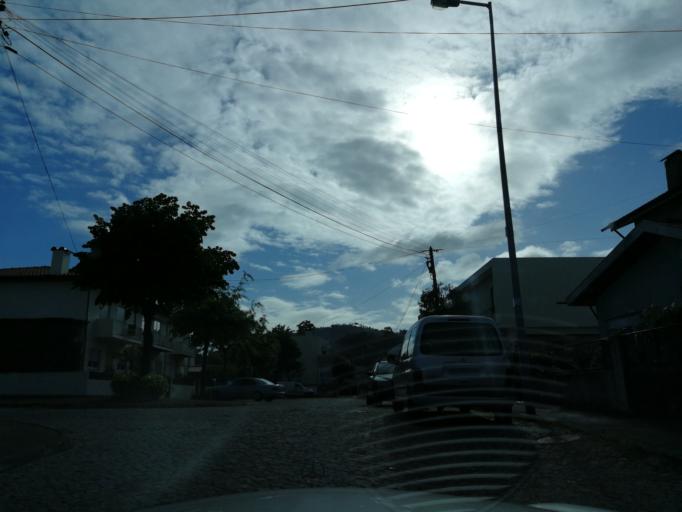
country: PT
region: Braga
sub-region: Braga
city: Braga
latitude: 41.5674
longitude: -8.4336
